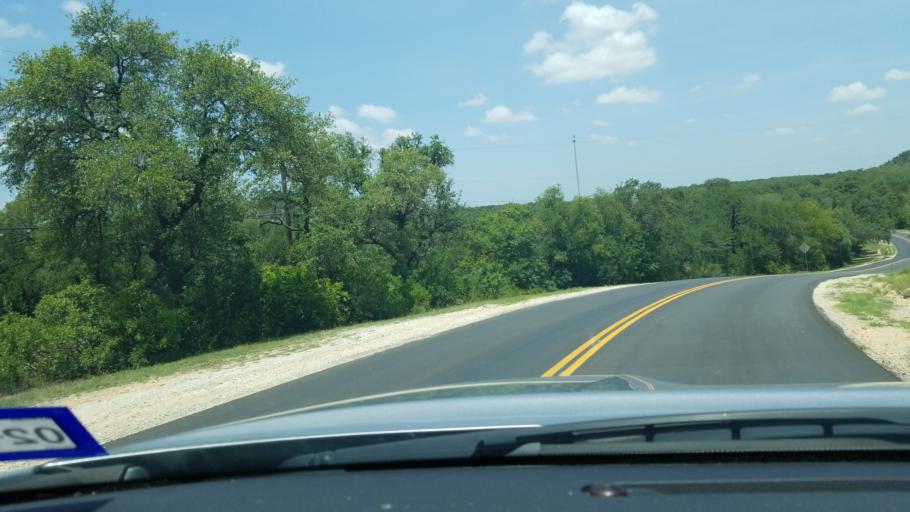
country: US
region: Texas
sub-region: Bexar County
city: Timberwood Park
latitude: 29.7045
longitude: -98.4562
